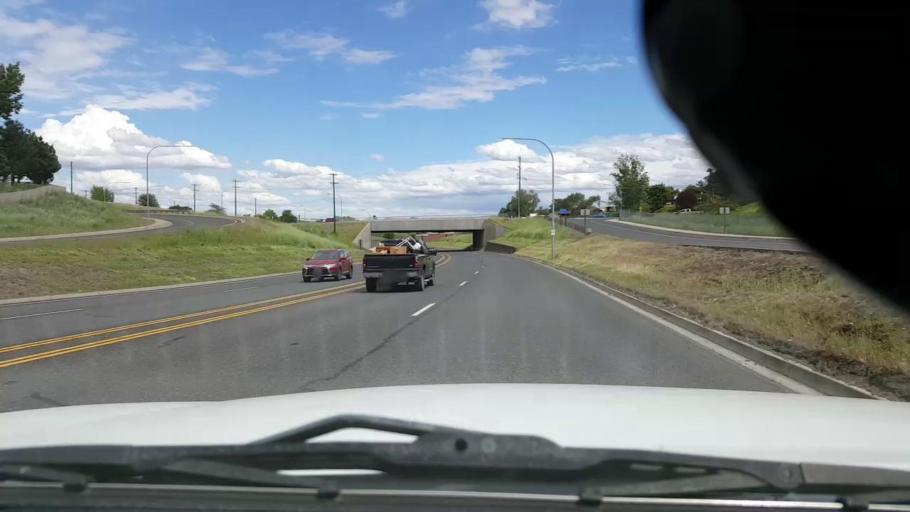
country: US
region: Washington
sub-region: Asotin County
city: West Clarkston-Highland
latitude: 46.4011
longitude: -117.0632
